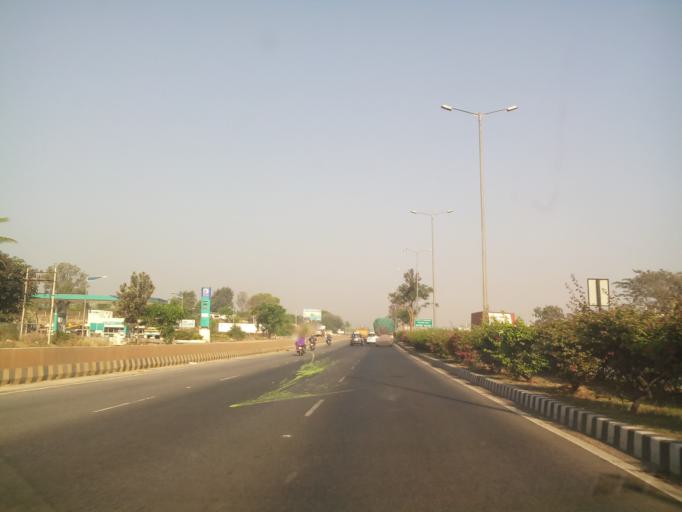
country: IN
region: Karnataka
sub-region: Bangalore Rural
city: Nelamangala
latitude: 13.0865
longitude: 77.4097
